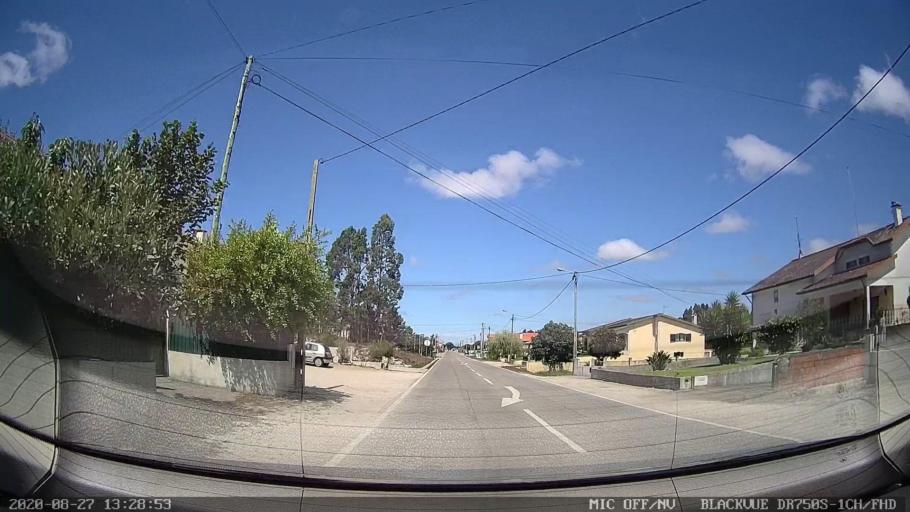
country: PT
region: Aveiro
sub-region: Vagos
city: Vagos
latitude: 40.5154
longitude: -8.6781
